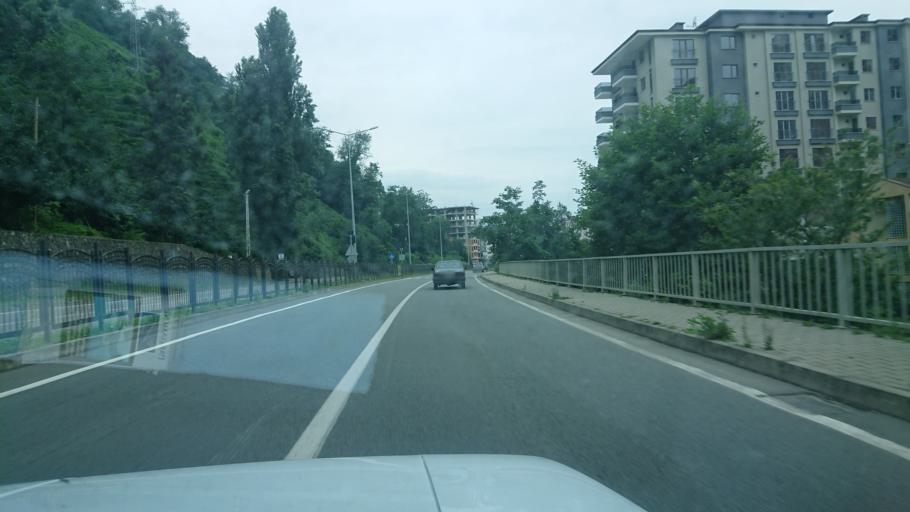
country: TR
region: Rize
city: Rize
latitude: 41.0283
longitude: 40.5553
